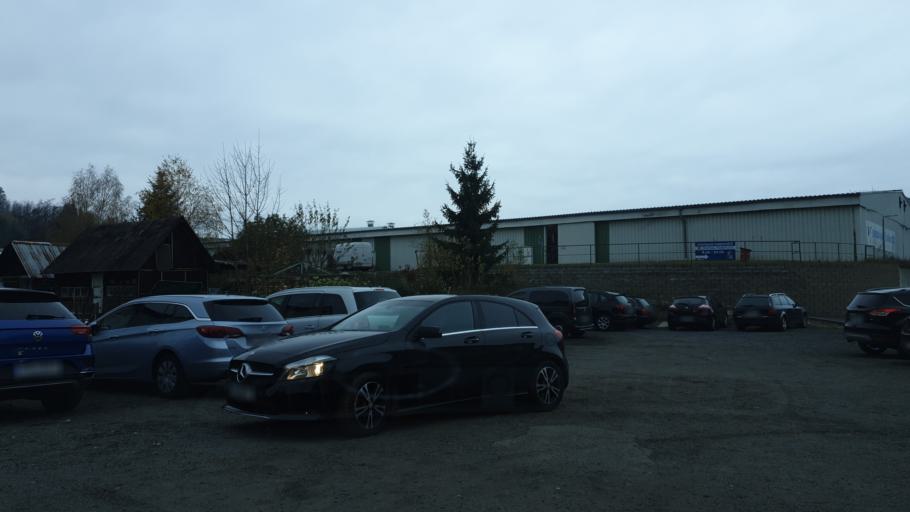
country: DE
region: Saxony
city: Johanngeorgenstadt
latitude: 50.4282
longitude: 12.7362
